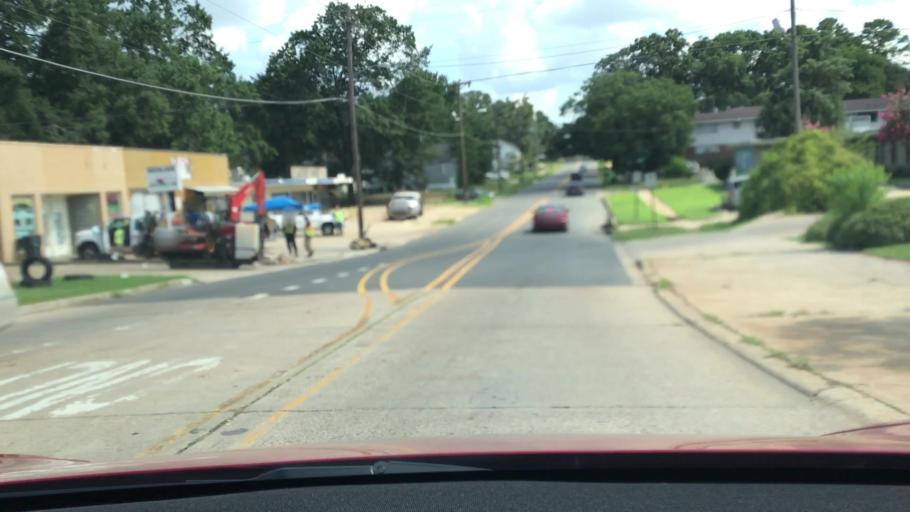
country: US
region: Louisiana
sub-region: Bossier Parish
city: Bossier City
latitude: 32.4925
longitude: -93.7333
